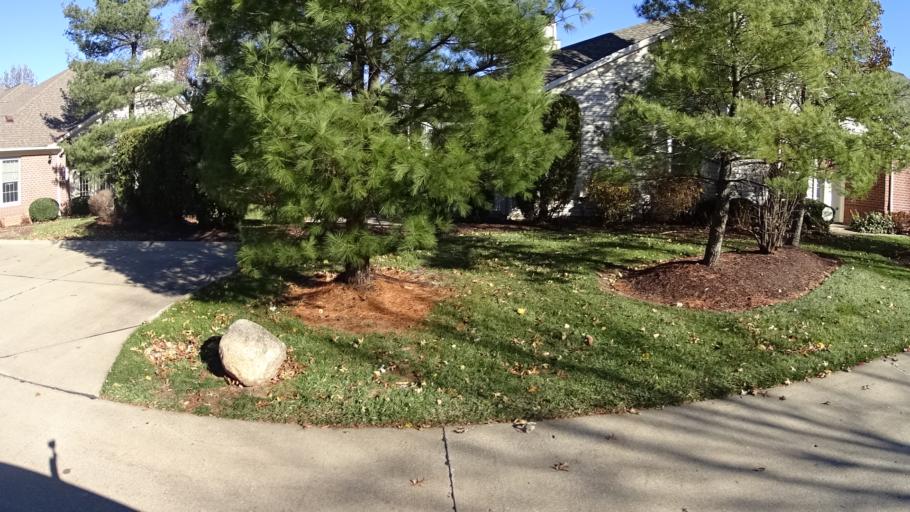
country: US
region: Ohio
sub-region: Lorain County
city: Avon Lake
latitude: 41.4943
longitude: -81.9777
